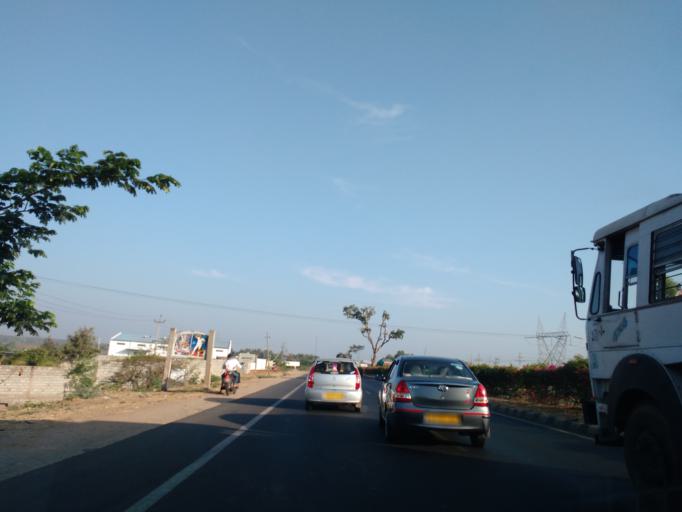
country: IN
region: Karnataka
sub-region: Bangalore Rural
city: Nelamangala
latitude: 13.1246
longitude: 77.3649
